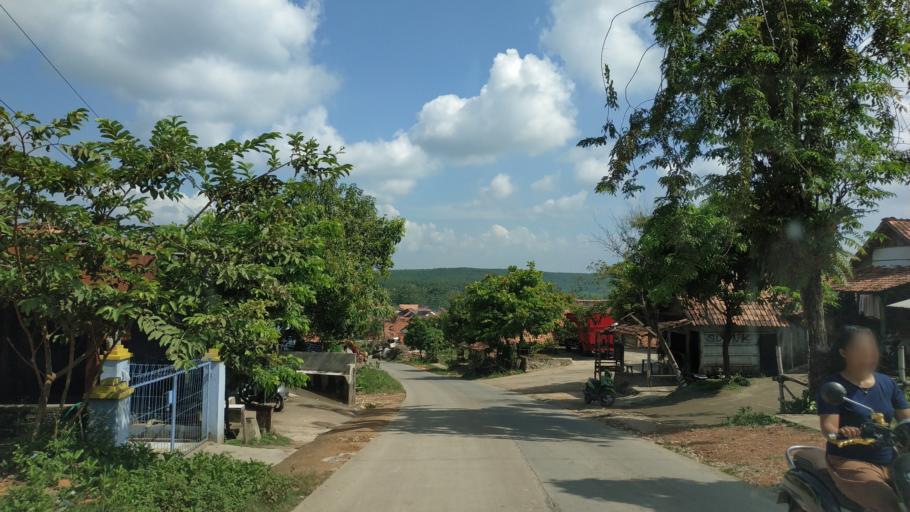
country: ID
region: Central Java
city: Jepang
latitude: -7.0117
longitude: 111.1175
